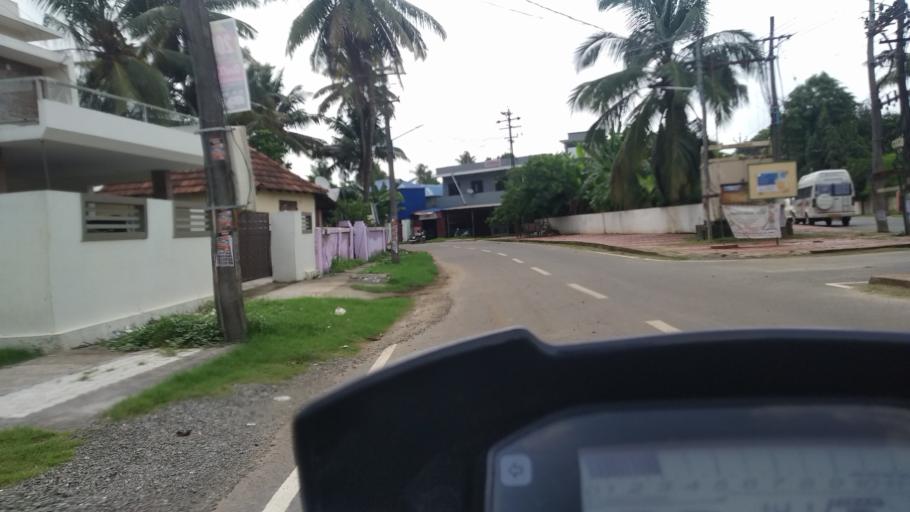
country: IN
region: Kerala
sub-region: Ernakulam
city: Aluva
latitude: 10.1176
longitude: 76.3500
